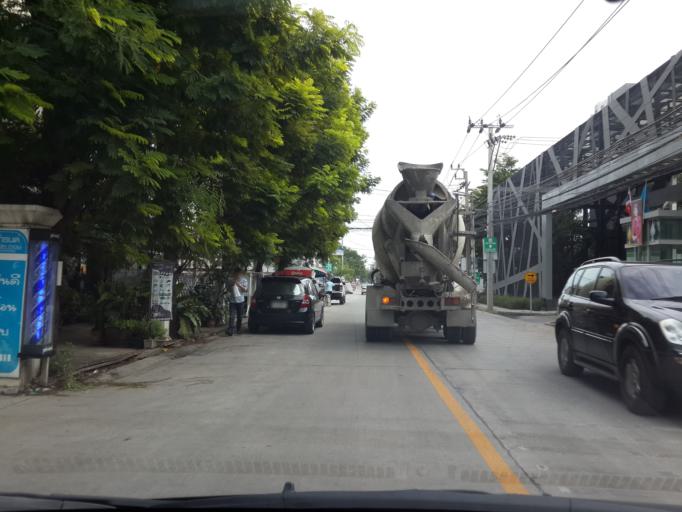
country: TH
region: Bangkok
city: Huai Khwang
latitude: 13.7722
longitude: 100.5966
